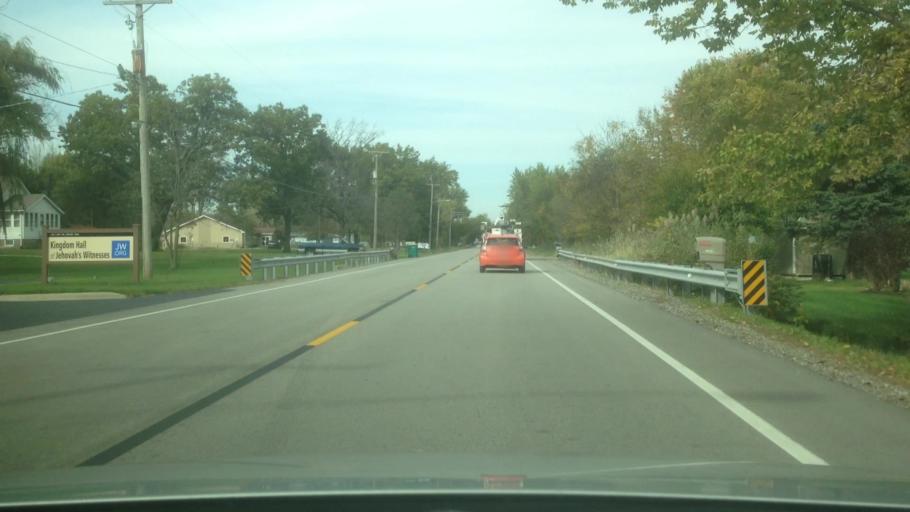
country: US
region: Illinois
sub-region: Will County
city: Wilmington
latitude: 41.3004
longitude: -88.1588
